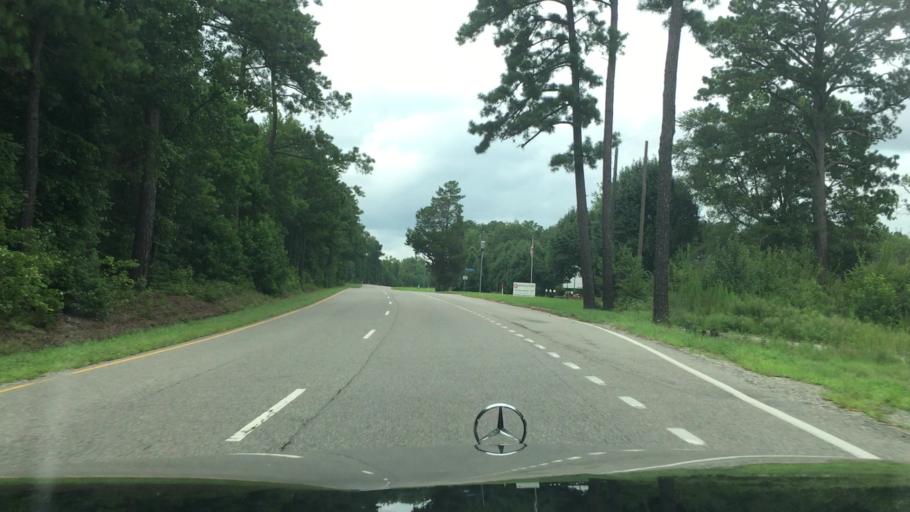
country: US
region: Virginia
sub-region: Chesterfield County
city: Woodlake
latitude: 37.3853
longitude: -77.8000
